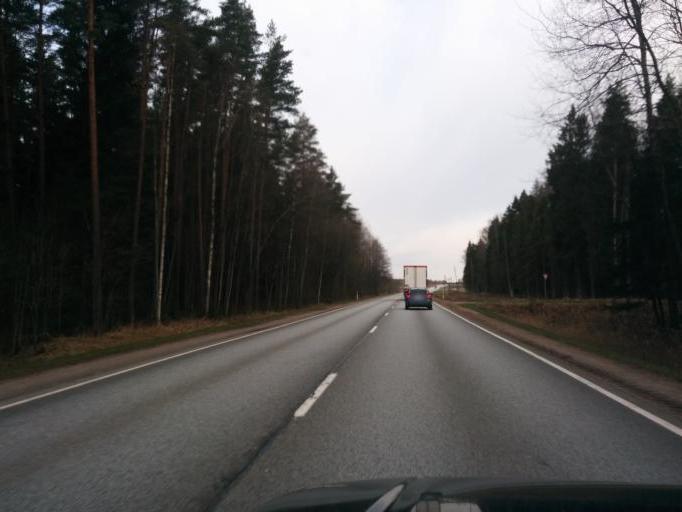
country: LV
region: Marupe
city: Marupe
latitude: 56.8295
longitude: 24.0514
